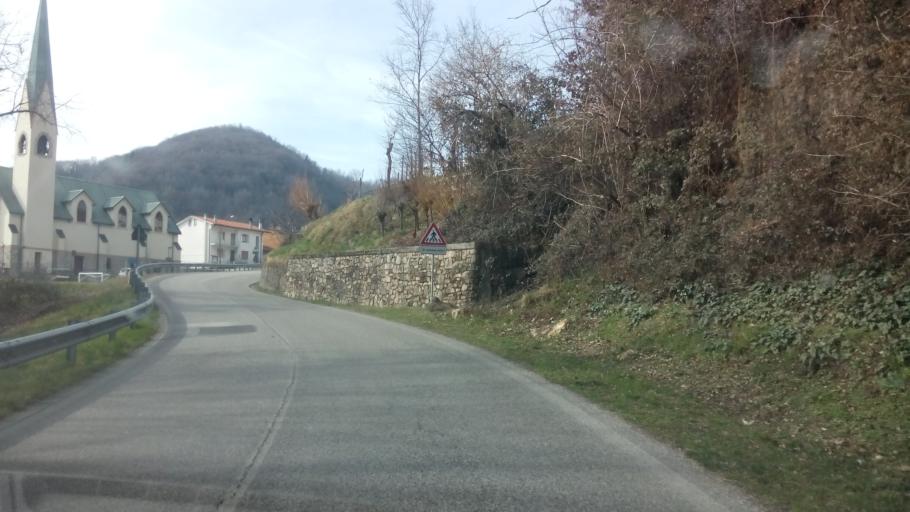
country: IT
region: Veneto
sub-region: Provincia di Vicenza
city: Schio
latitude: 45.7412
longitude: 11.3548
